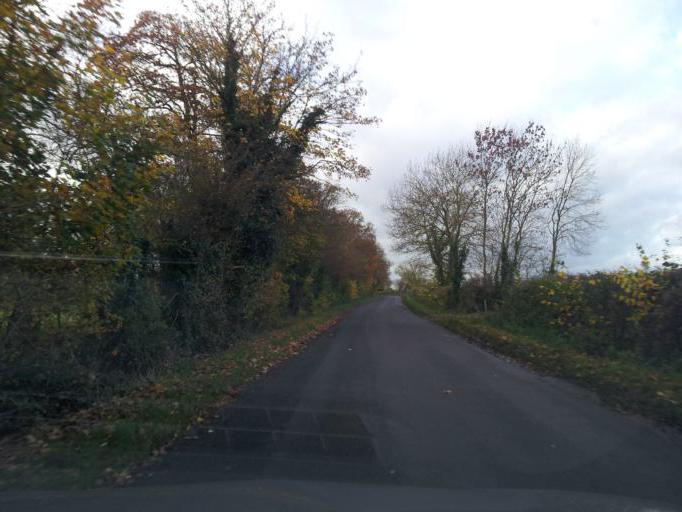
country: GB
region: England
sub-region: Lincolnshire
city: Long Bennington
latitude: 52.9832
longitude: -0.7881
